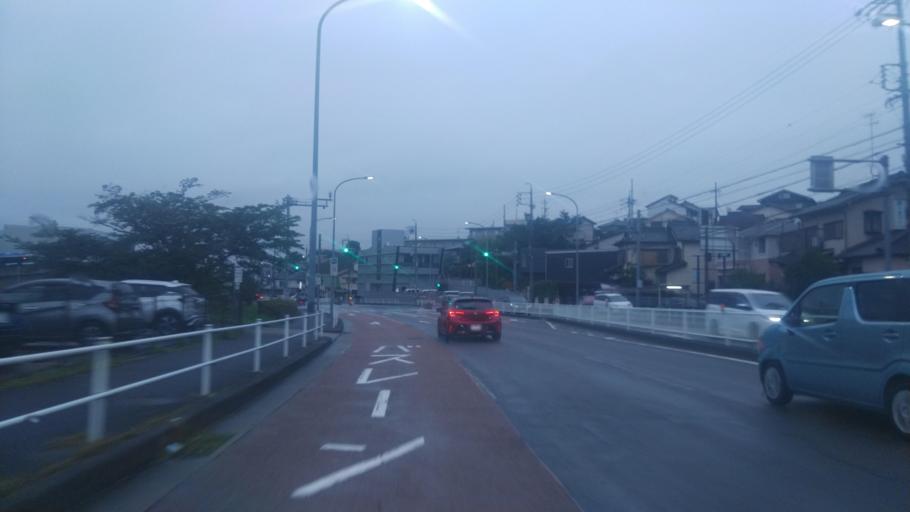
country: JP
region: Aichi
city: Kasugai
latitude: 35.2205
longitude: 136.9840
